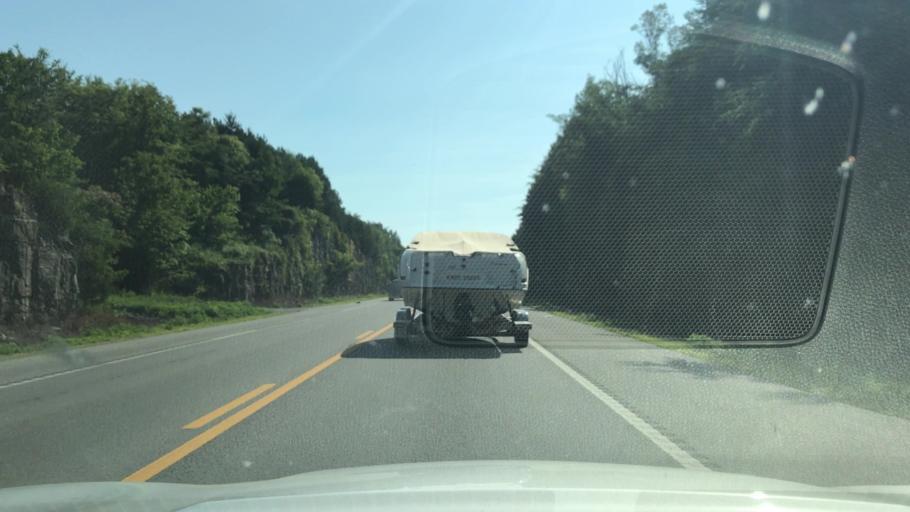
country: US
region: Tennessee
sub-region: Pickett County
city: Byrdstown
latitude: 36.6080
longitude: -85.1129
